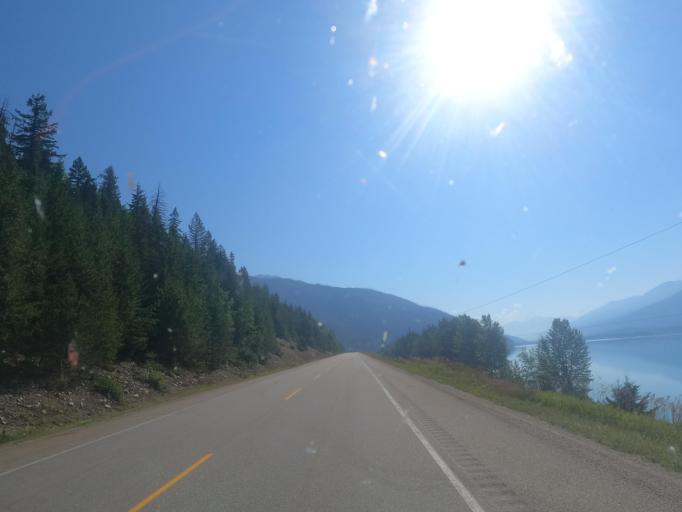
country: CA
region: Alberta
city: Jasper Park Lodge
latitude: 52.9550
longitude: -118.8868
